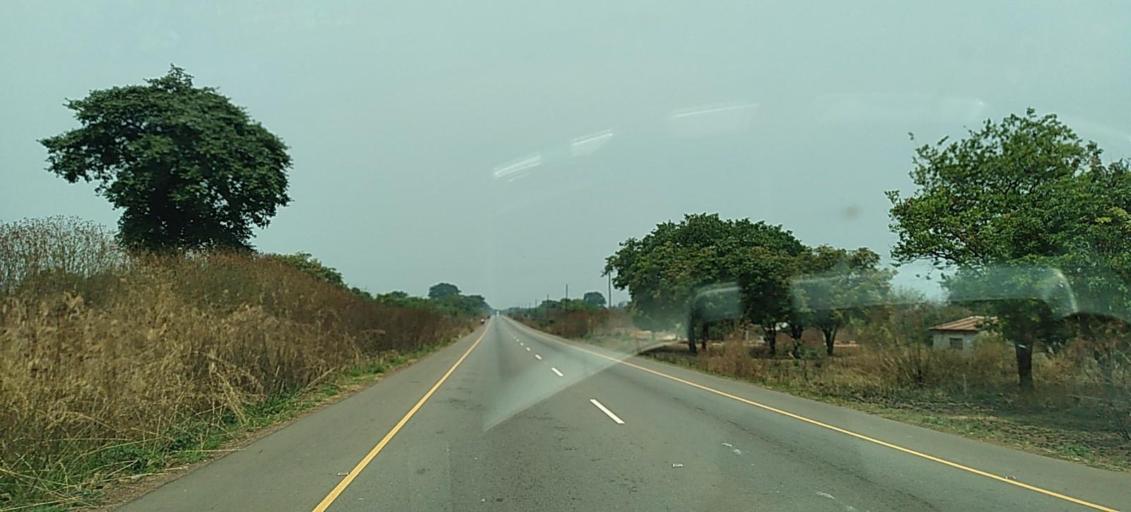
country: ZM
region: Copperbelt
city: Chililabombwe
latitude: -12.5066
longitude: 27.5476
